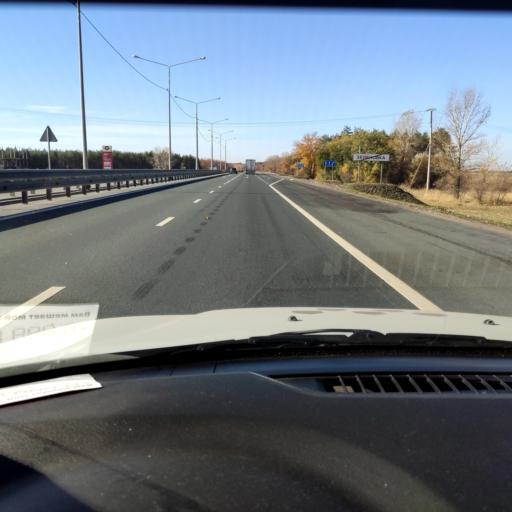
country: RU
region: Samara
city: Zhigulevsk
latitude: 53.5136
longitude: 49.5941
